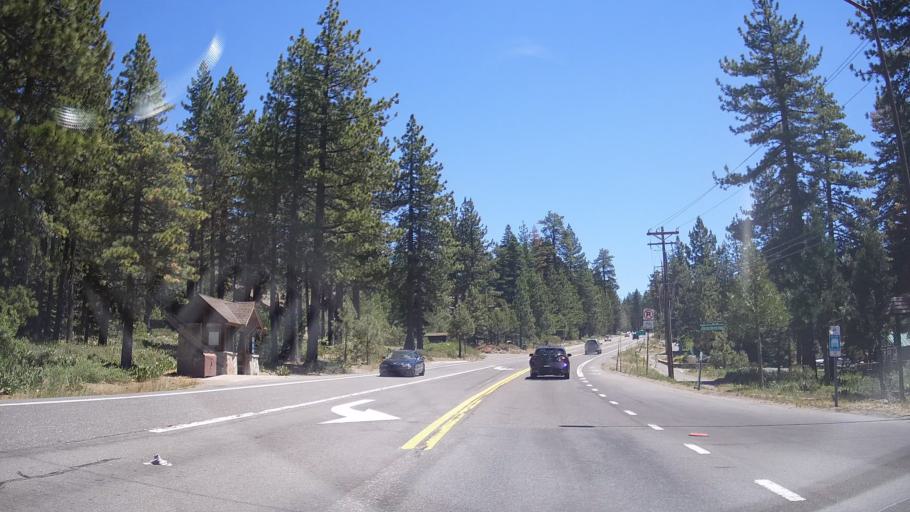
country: US
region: California
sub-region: Placer County
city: Dollar Point
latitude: 39.1898
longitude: -120.1134
